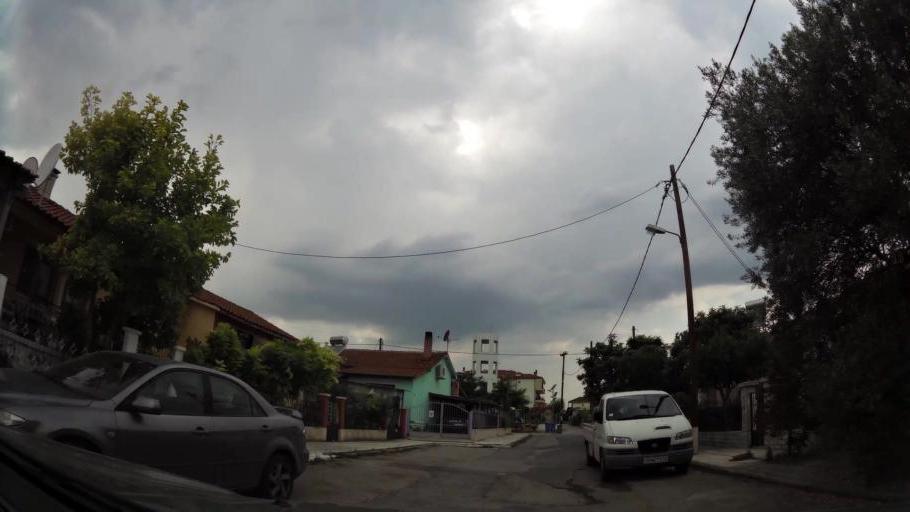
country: GR
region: Central Macedonia
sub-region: Nomos Imathias
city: Veroia
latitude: 40.5316
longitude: 22.2092
